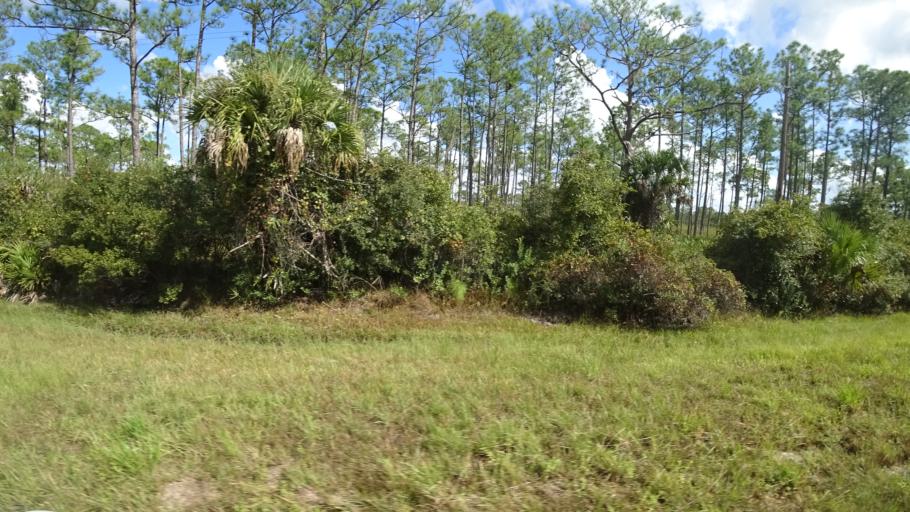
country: US
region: Florida
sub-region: Sarasota County
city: North Port
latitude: 27.2437
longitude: -82.1219
